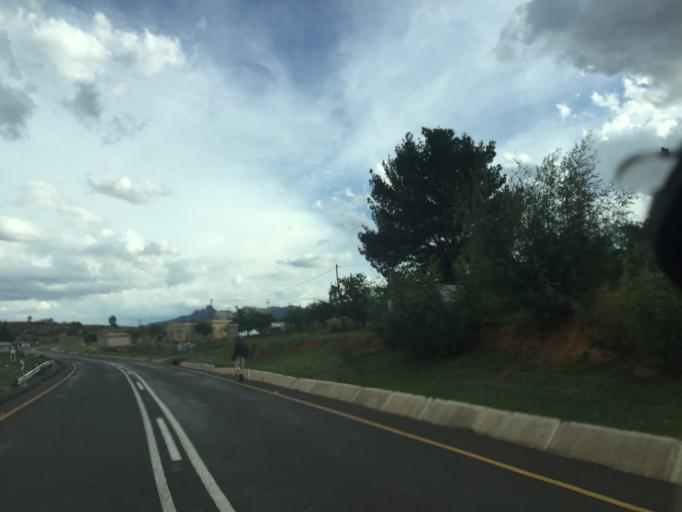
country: LS
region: Berea
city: Teyateyaneng
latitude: -29.1334
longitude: 27.9876
